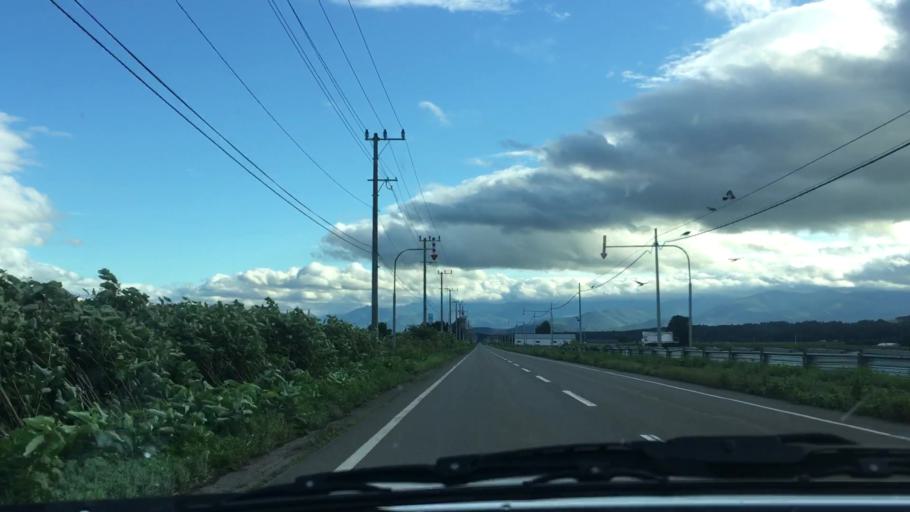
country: JP
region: Hokkaido
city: Otofuke
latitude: 43.1577
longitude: 142.9031
